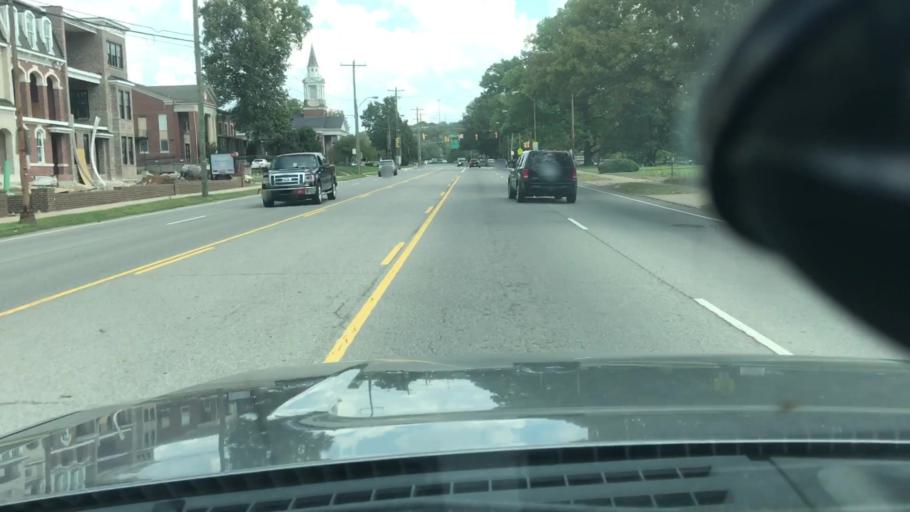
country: US
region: Tennessee
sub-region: Davidson County
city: Belle Meade
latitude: 36.1340
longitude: -86.8268
